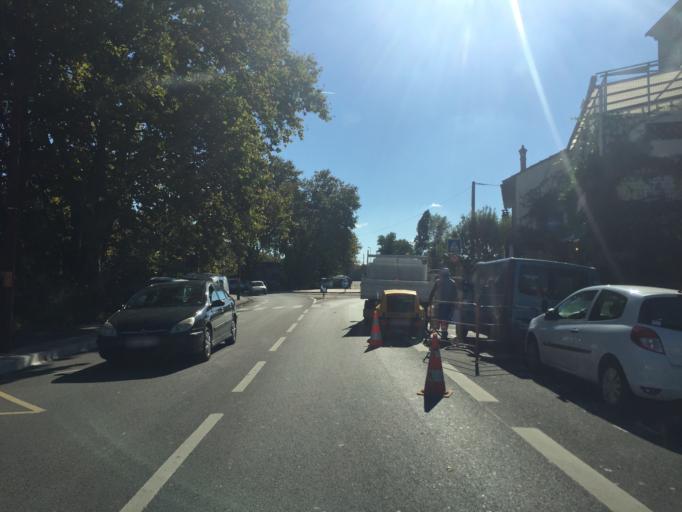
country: FR
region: Provence-Alpes-Cote d'Azur
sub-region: Departement du Vaucluse
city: Avignon
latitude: 43.9429
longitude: 4.8208
